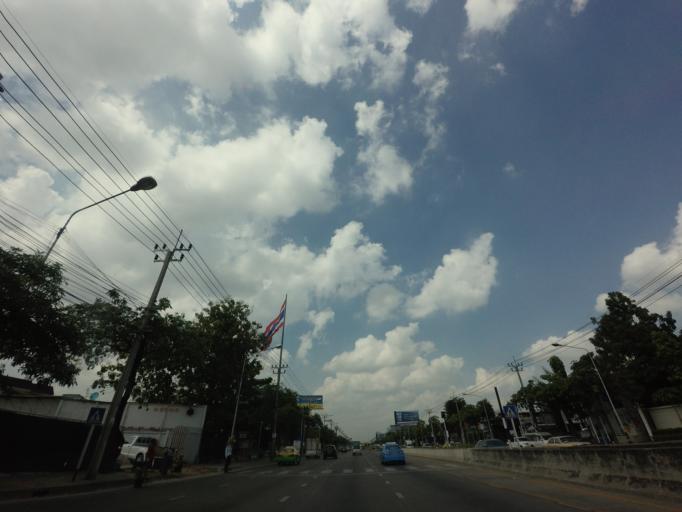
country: TH
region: Bangkok
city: Lat Phrao
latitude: 13.8172
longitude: 100.6394
